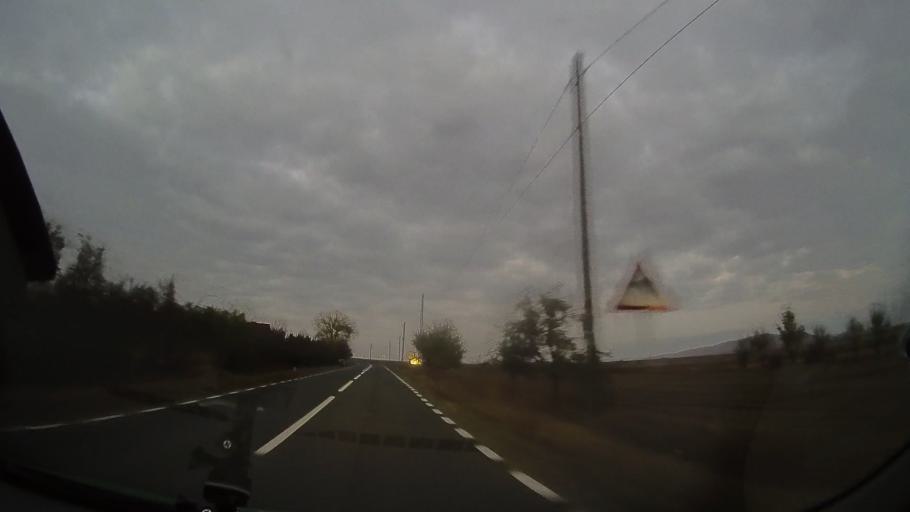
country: RO
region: Tulcea
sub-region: Comuna Nalbant
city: Nicolae Balcescu
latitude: 45.0011
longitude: 28.5943
